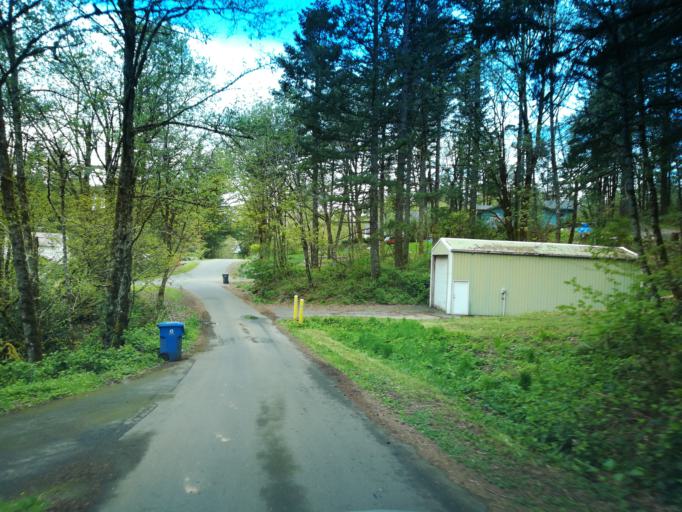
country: US
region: Oregon
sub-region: Clackamas County
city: Damascus
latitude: 45.4551
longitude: -122.4572
